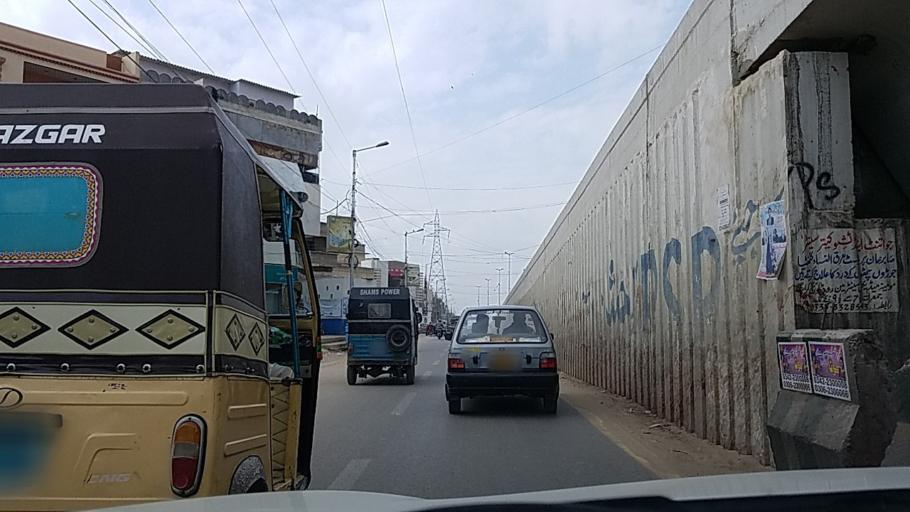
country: PK
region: Sindh
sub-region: Karachi District
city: Karachi
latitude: 24.8176
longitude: 67.1069
